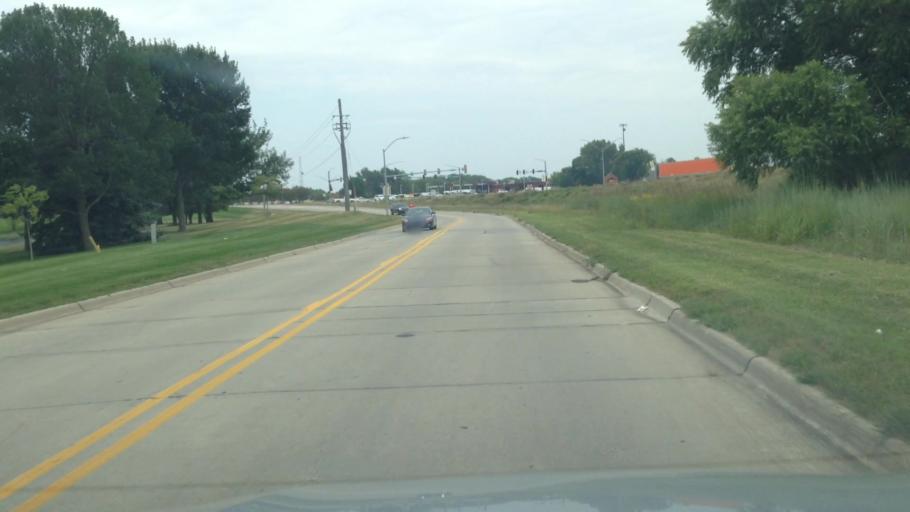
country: US
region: Iowa
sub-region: Polk County
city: Clive
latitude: 41.6304
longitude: -93.7741
